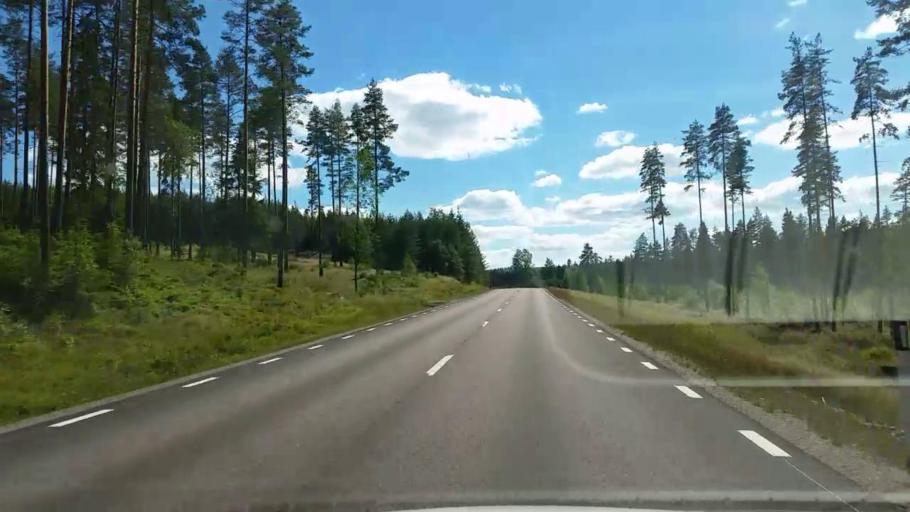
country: SE
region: Dalarna
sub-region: Faluns Kommun
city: Svardsjo
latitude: 60.7648
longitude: 15.7548
